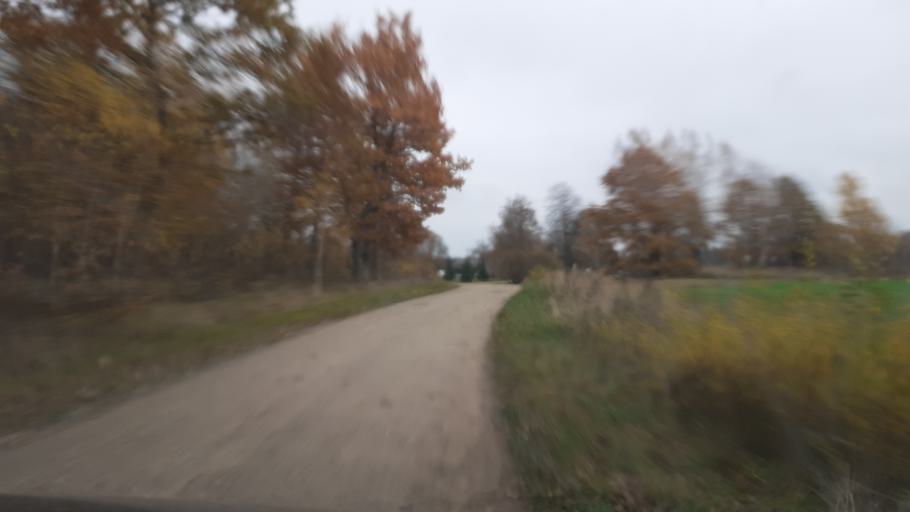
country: LV
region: Saldus Rajons
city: Saldus
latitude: 56.8600
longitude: 22.3392
